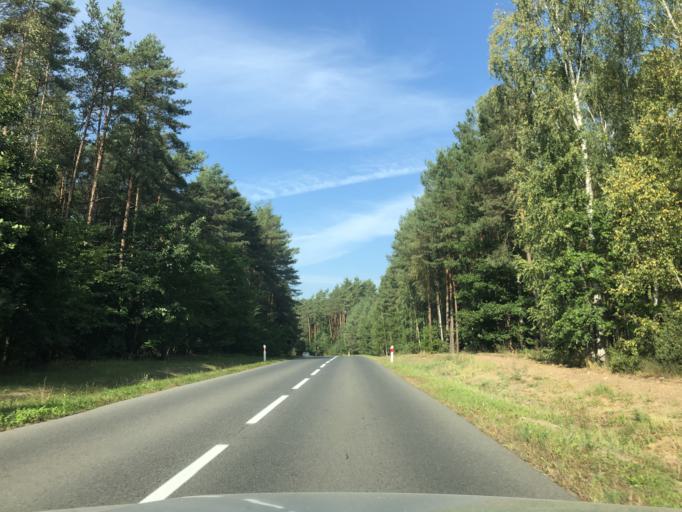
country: PL
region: Greater Poland Voivodeship
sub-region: Powiat pilski
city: Kaczory
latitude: 53.1169
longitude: 16.8303
